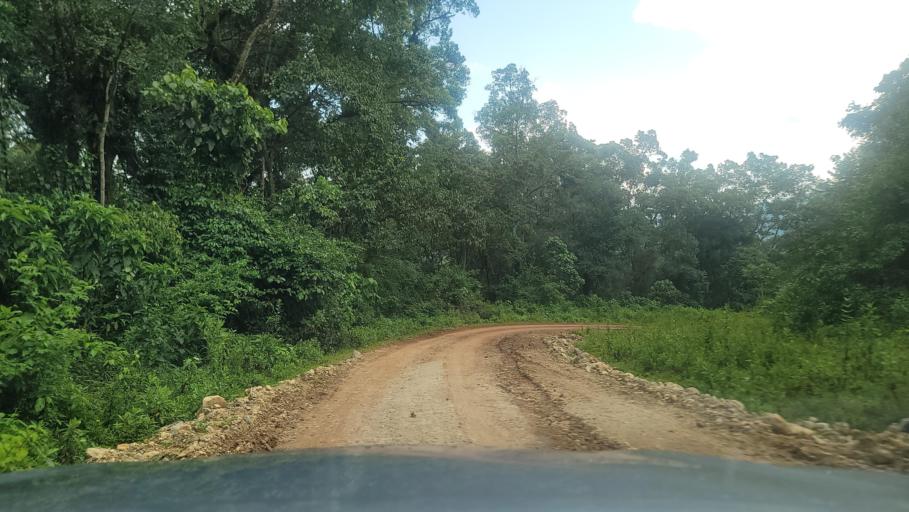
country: ET
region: Southern Nations, Nationalities, and People's Region
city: Bonga
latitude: 7.6229
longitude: 36.2106
